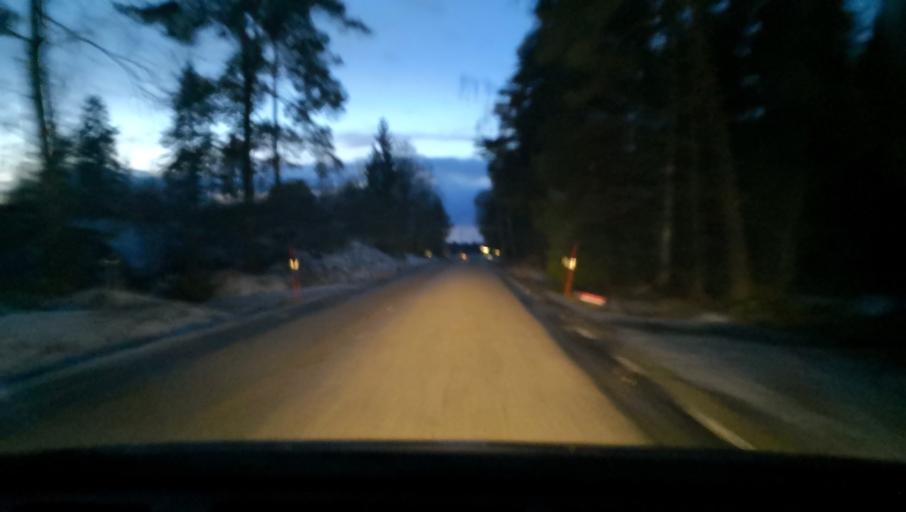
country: SE
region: Vaestmanland
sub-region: Sala Kommun
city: Sala
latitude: 59.8539
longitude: 16.4763
